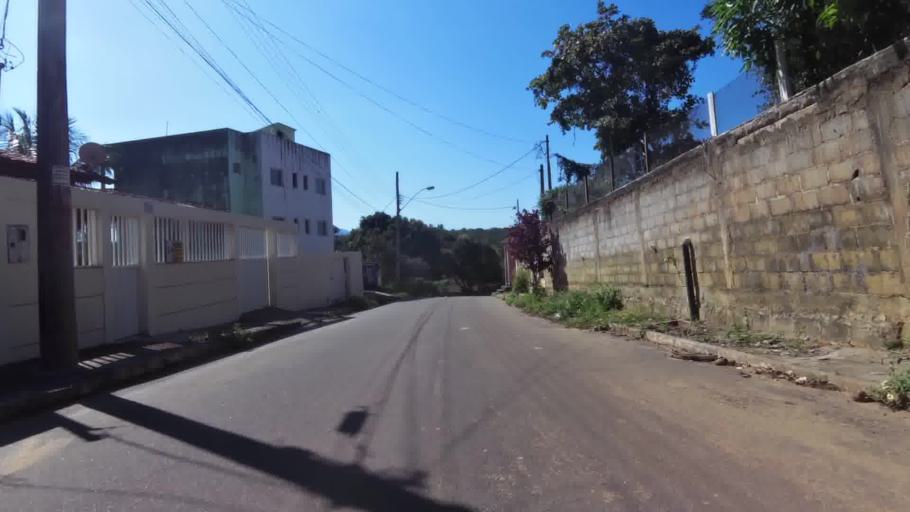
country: BR
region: Espirito Santo
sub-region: Guarapari
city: Guarapari
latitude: -20.7329
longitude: -40.5459
